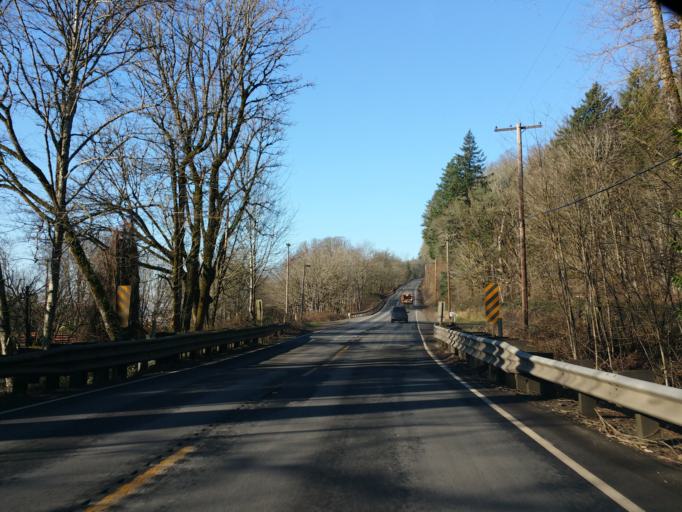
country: US
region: Washington
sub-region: Clark County
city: Washougal
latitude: 45.5615
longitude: -122.2668
